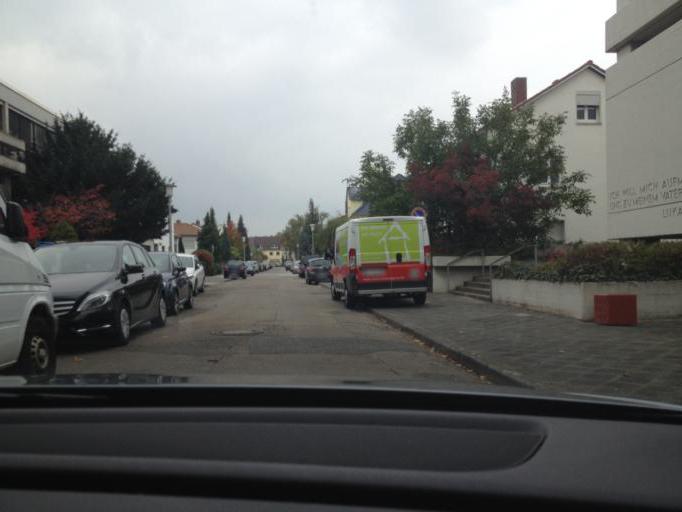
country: DE
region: Rheinland-Pfalz
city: Altrip
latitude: 49.4600
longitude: 8.4874
